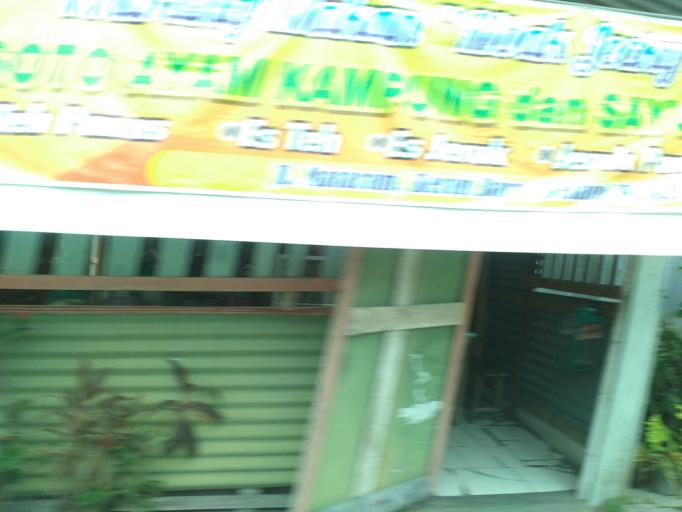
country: ID
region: Central Java
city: Klaten
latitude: -7.6885
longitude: 110.6345
